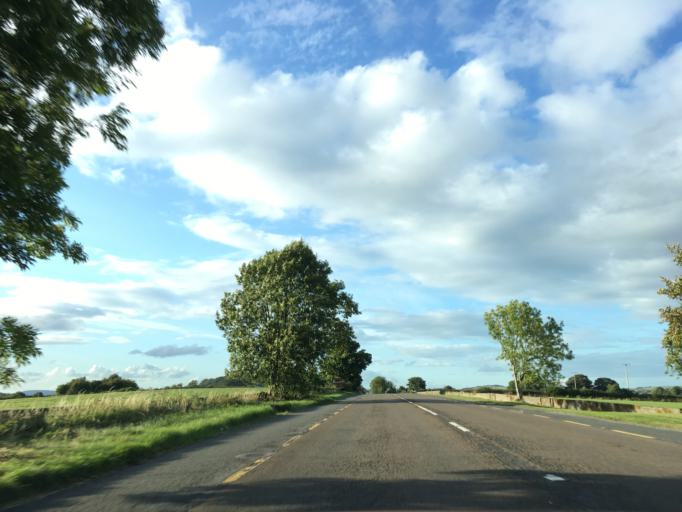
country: IE
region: Munster
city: Cashel
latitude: 52.4909
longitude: -7.8903
